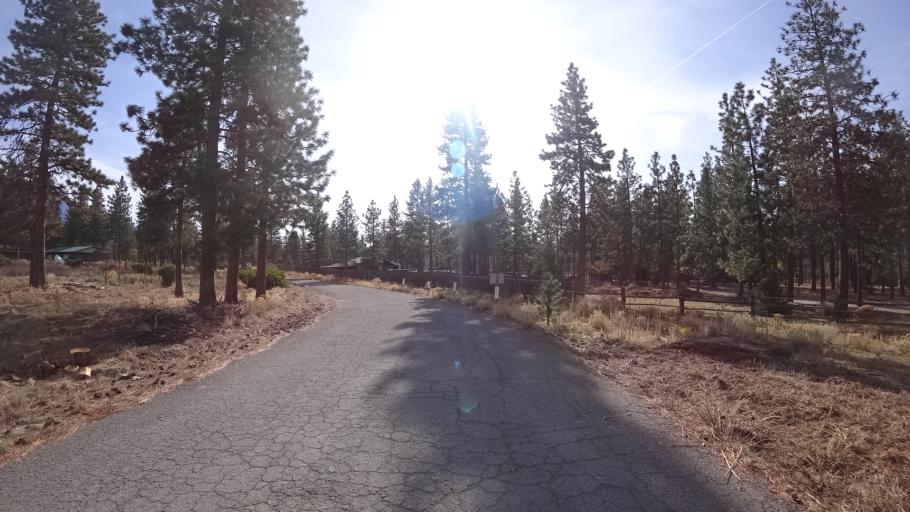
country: US
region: California
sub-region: Siskiyou County
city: Weed
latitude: 41.4937
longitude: -122.3744
